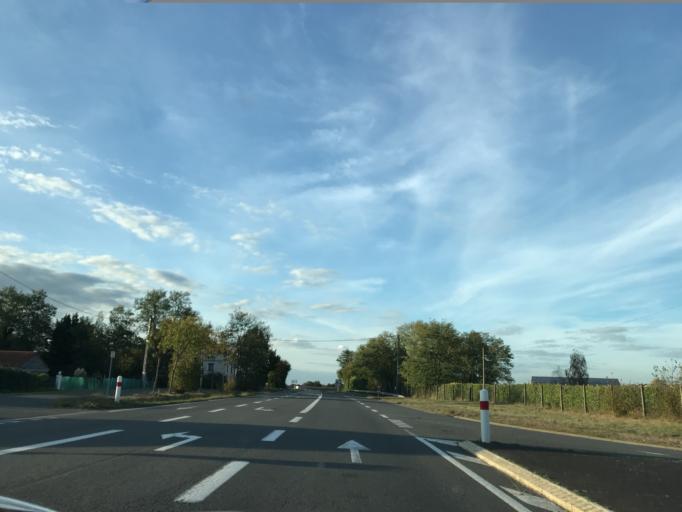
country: FR
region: Auvergne
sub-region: Departement de l'Allier
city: Saint-Yorre
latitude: 46.0409
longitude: 3.4741
